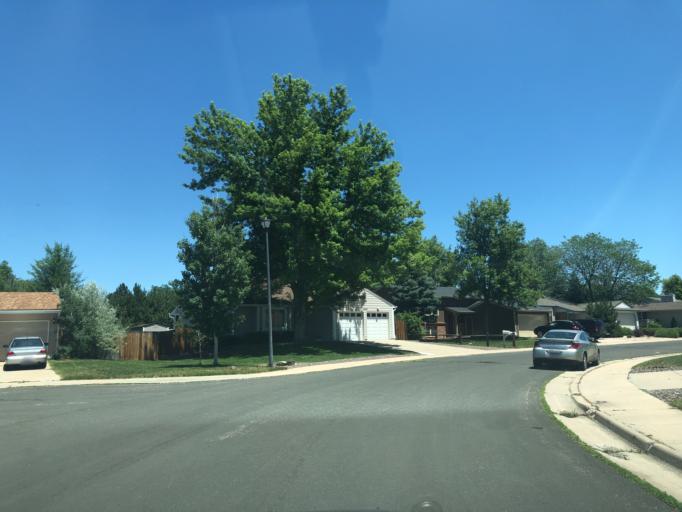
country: US
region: Colorado
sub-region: Arapahoe County
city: Dove Valley
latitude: 39.6196
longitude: -104.7774
